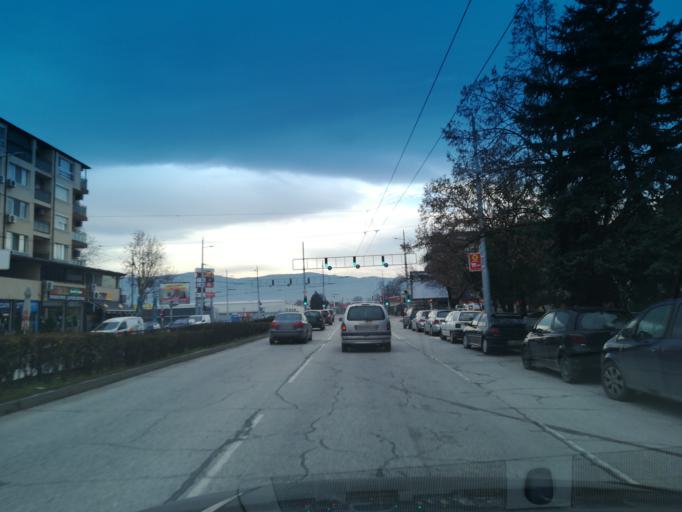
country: BG
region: Plovdiv
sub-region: Obshtina Plovdiv
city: Plovdiv
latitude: 42.1263
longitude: 24.7206
